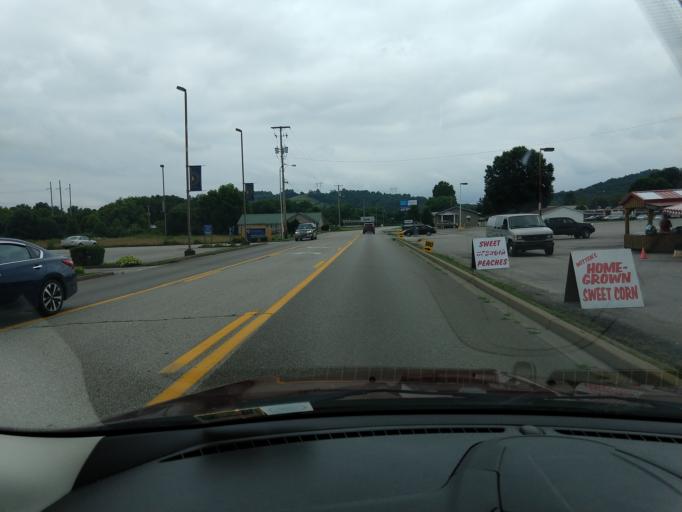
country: US
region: West Virginia
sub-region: Jackson County
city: Ripley
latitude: 38.8242
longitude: -81.7239
